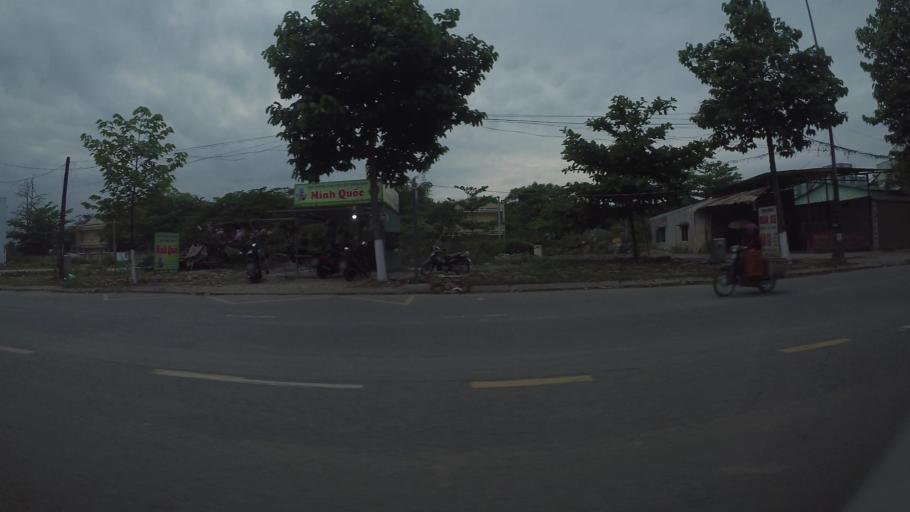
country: VN
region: Da Nang
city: Lien Chieu
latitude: 16.0731
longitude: 108.1106
